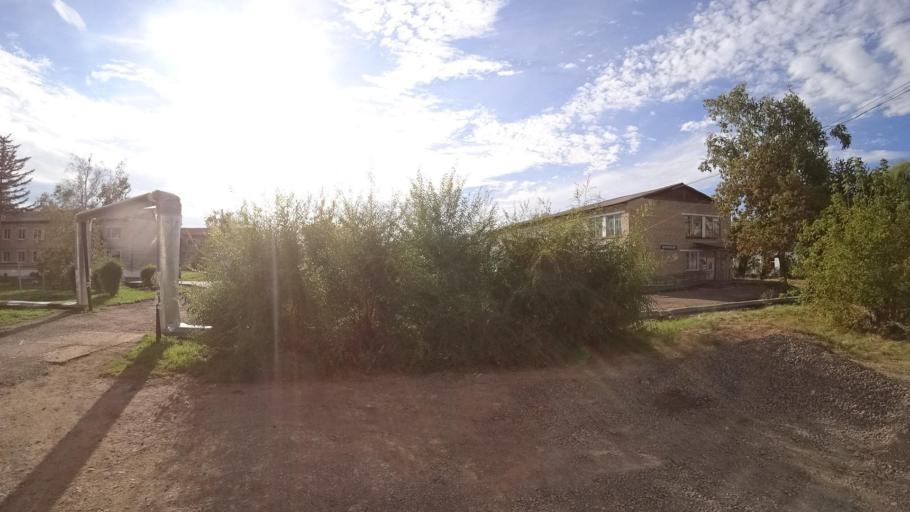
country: RU
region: Primorskiy
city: Dostoyevka
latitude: 44.2911
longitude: 133.4253
